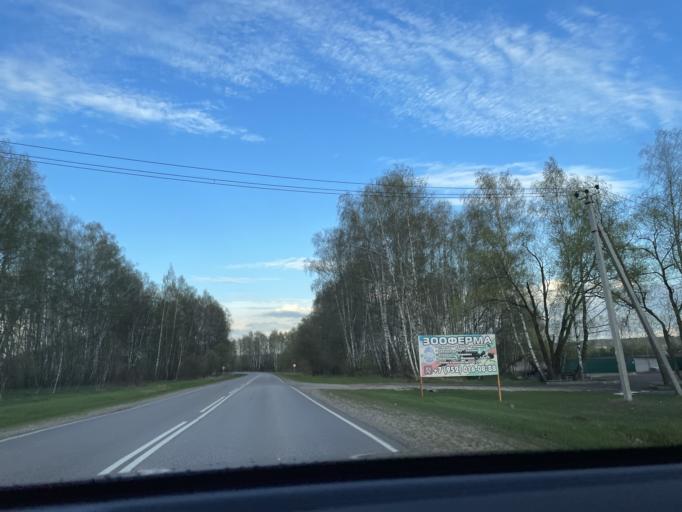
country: RU
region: Tula
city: Novogurovskiy
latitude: 54.5191
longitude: 37.2397
